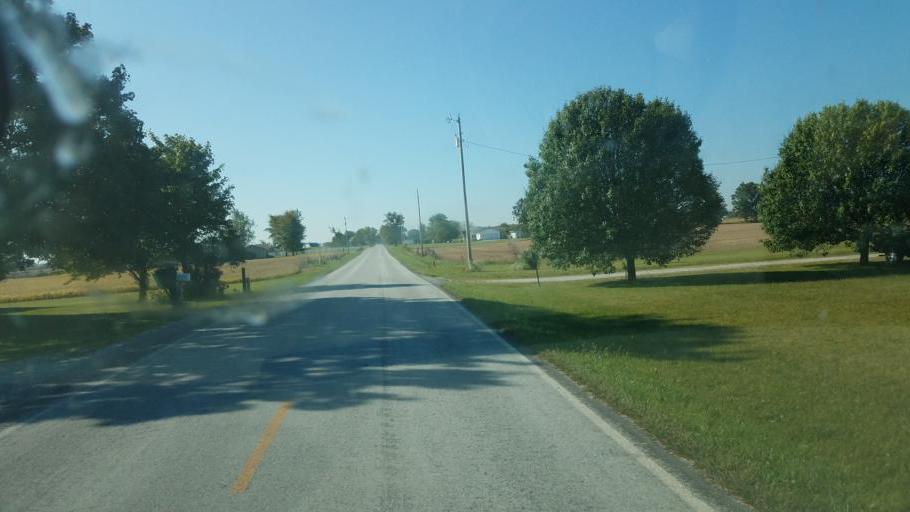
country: US
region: Ohio
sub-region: Hardin County
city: Kenton
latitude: 40.6197
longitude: -83.5805
